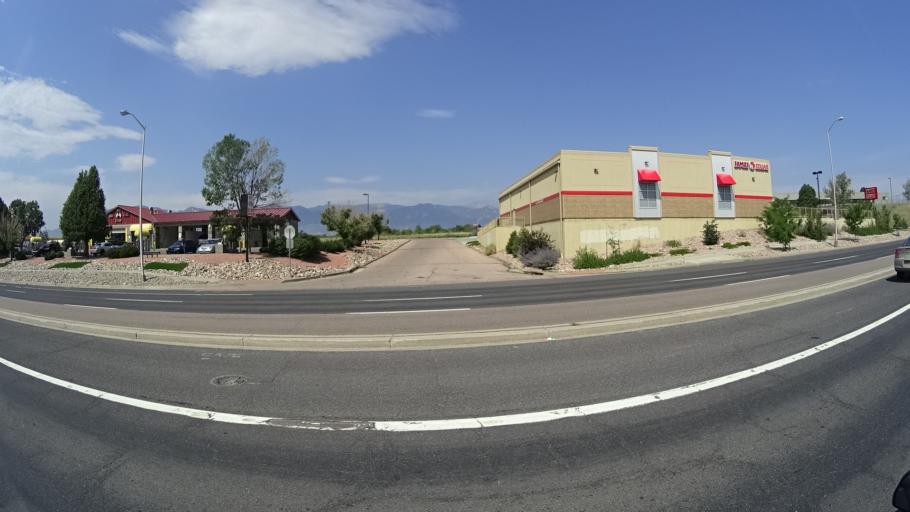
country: US
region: Colorado
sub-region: El Paso County
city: Stratmoor
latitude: 38.8108
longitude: -104.7574
